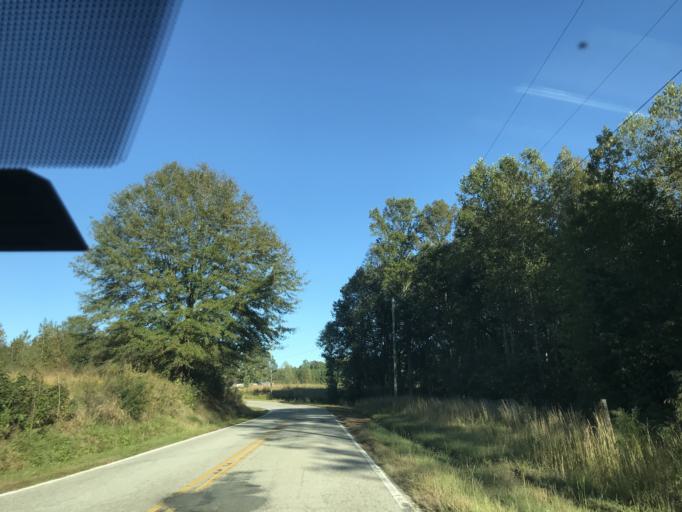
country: US
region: South Carolina
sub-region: Spartanburg County
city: Mayo
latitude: 35.1216
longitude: -81.7928
